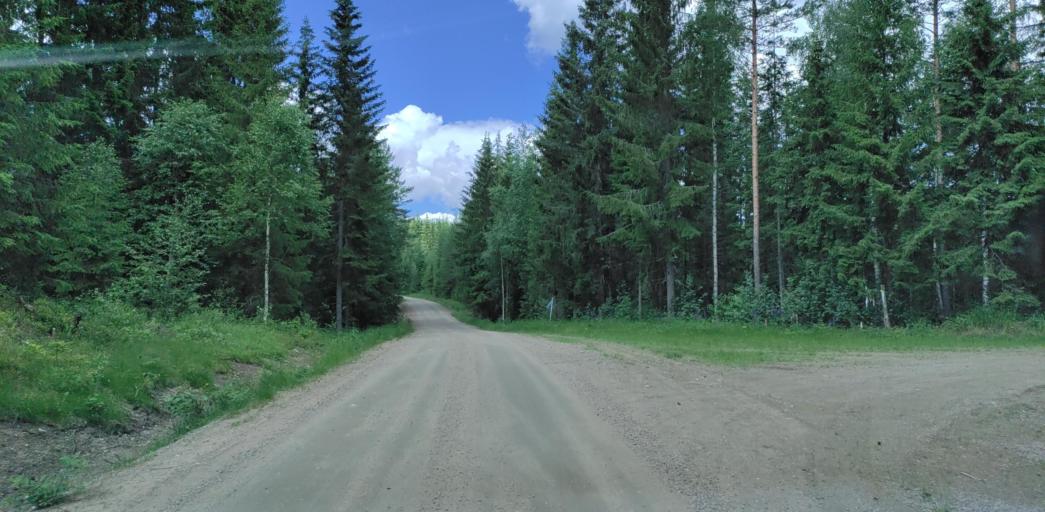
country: SE
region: Vaermland
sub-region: Hagfors Kommun
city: Ekshaerad
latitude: 60.1007
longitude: 13.3901
